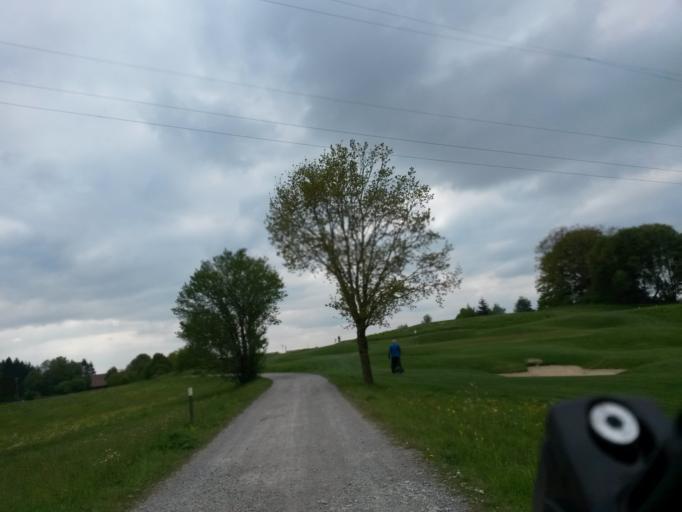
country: DE
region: Baden-Wuerttemberg
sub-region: Tuebingen Region
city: Bad Waldsee
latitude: 47.9348
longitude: 9.7764
